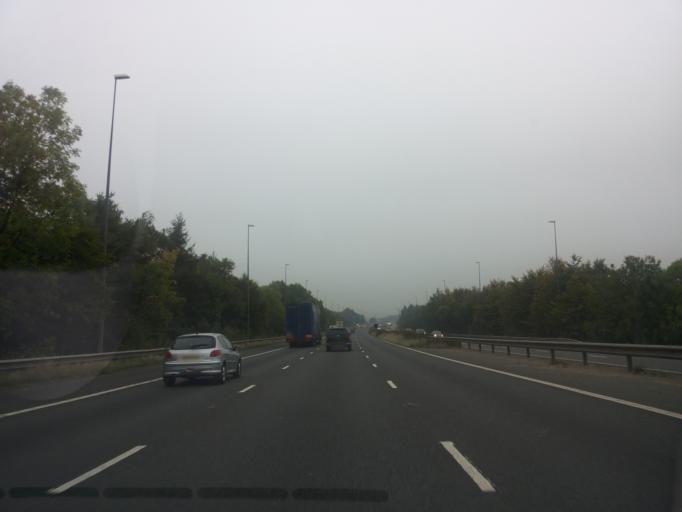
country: GB
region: England
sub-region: Borough of Bury
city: Whitefield
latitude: 53.5694
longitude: -2.2711
